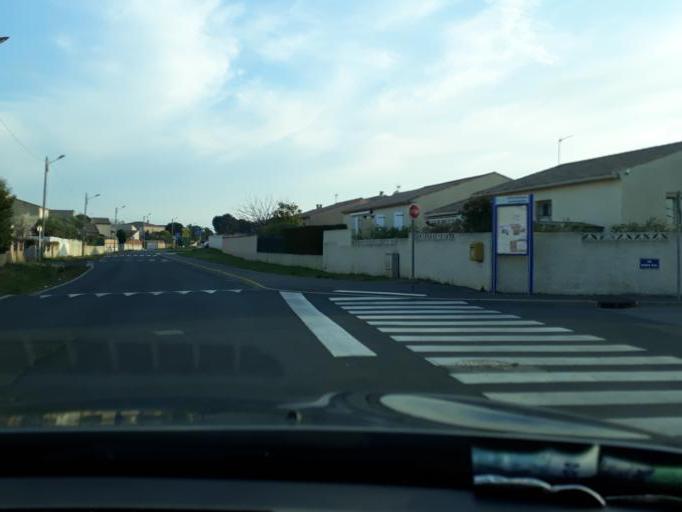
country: FR
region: Languedoc-Roussillon
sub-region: Departement de l'Herault
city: Marseillan
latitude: 43.3398
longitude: 3.5331
